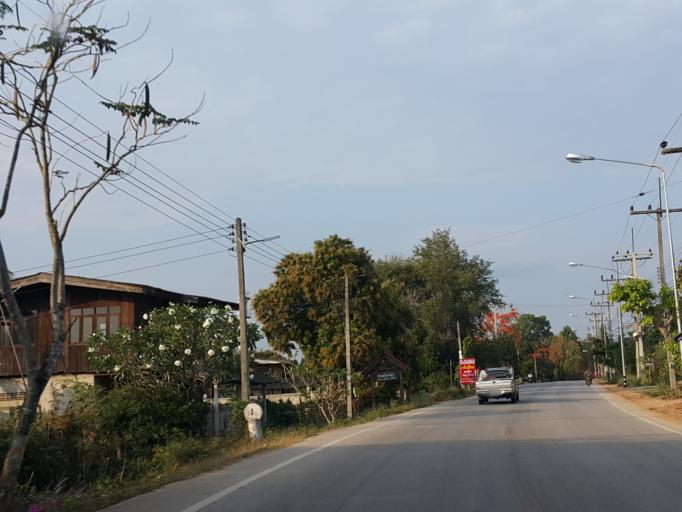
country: TH
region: Lampang
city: Chae Hom
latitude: 18.5384
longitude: 99.4790
